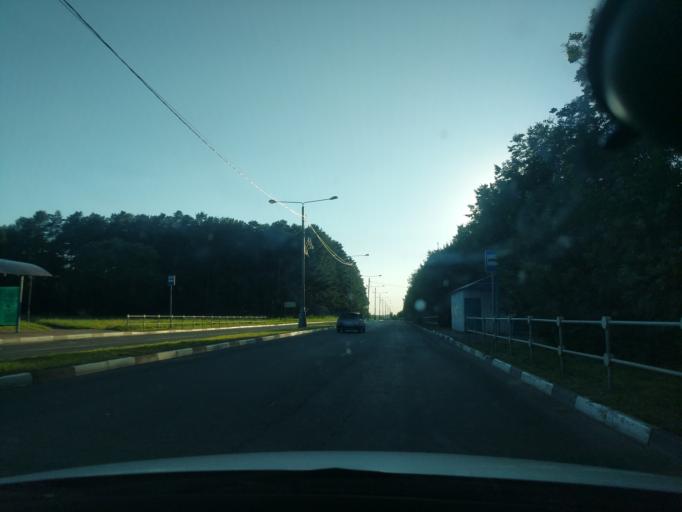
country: RU
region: Moskovskaya
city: Pushchino
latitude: 54.8333
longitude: 37.6123
